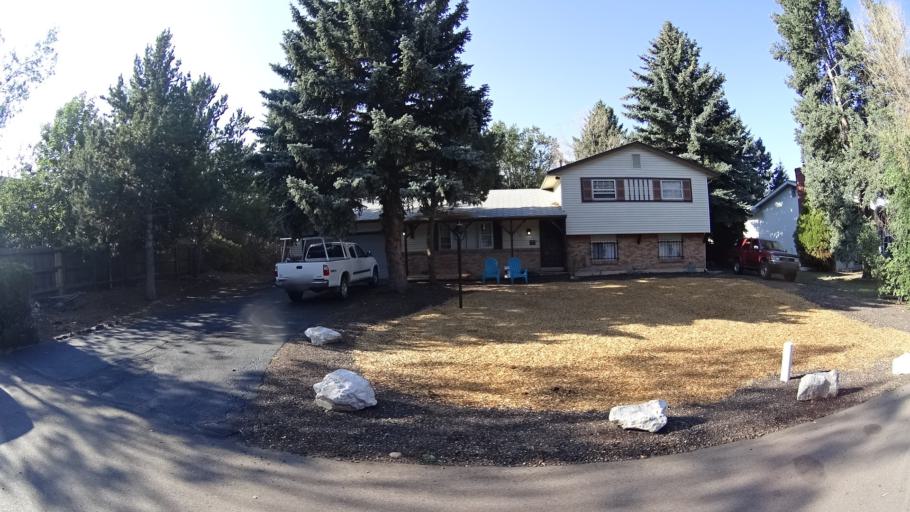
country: US
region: Colorado
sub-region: El Paso County
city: Air Force Academy
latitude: 38.9315
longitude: -104.7821
